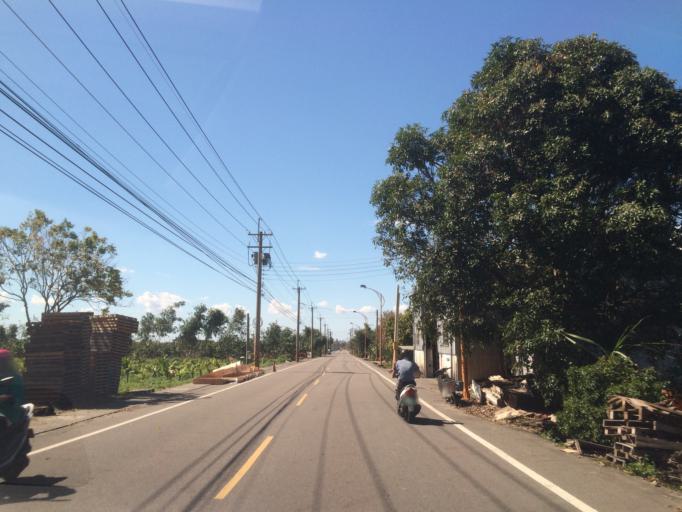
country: TW
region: Taiwan
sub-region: Yunlin
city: Douliu
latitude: 23.7032
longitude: 120.5919
